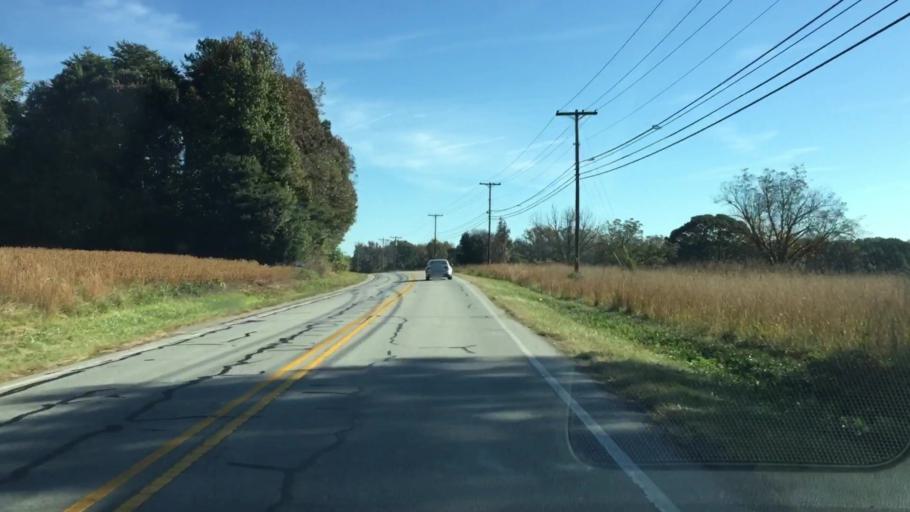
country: US
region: North Carolina
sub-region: Rowan County
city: China Grove
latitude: 35.6532
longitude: -80.5728
